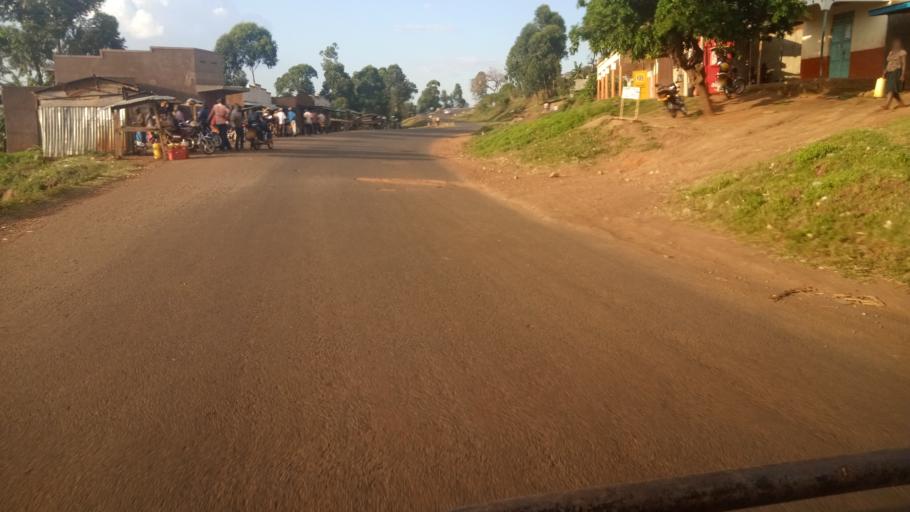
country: UG
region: Eastern Region
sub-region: Kapchorwa District
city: Kapchorwa
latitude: 1.3389
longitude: 34.3593
